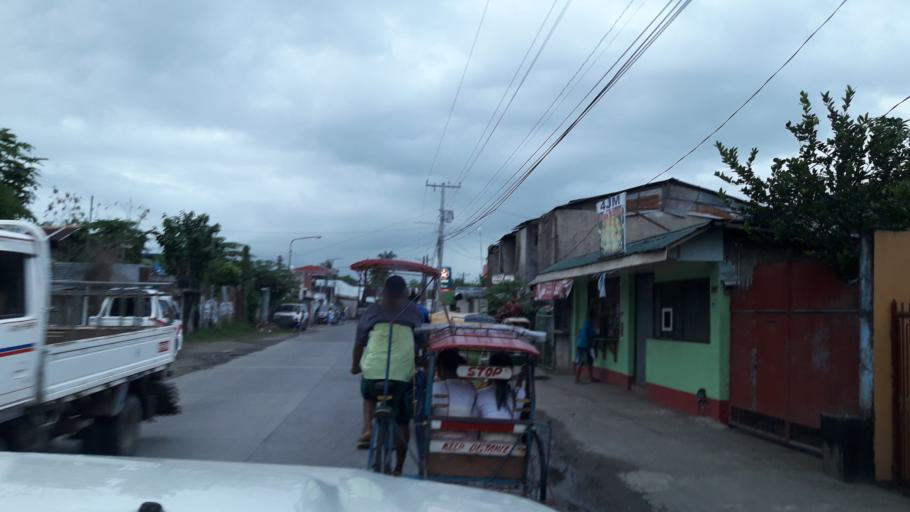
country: PH
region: Eastern Visayas
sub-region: Province of Leyte
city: Panalanoy
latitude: 11.2183
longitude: 125.0028
